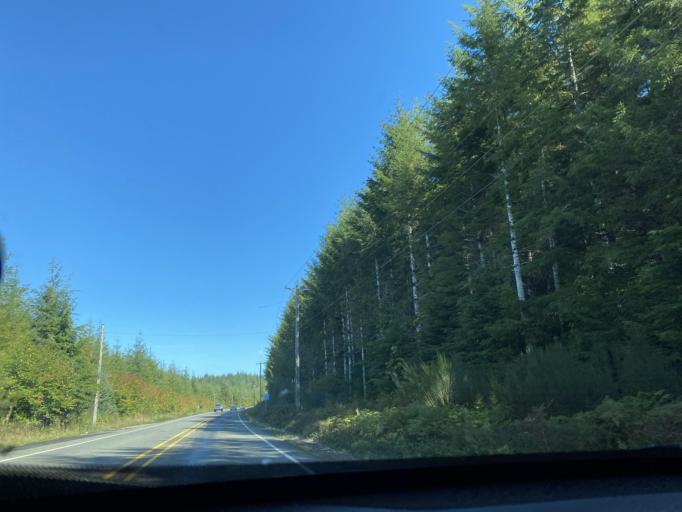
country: US
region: Washington
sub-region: Clallam County
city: Forks
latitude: 47.9608
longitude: -124.4453
